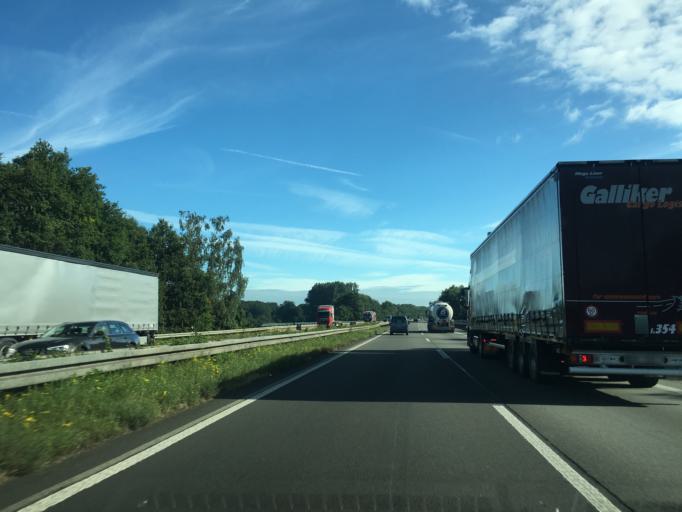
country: DE
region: North Rhine-Westphalia
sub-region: Regierungsbezirk Munster
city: Greven
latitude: 52.0759
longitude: 7.6347
